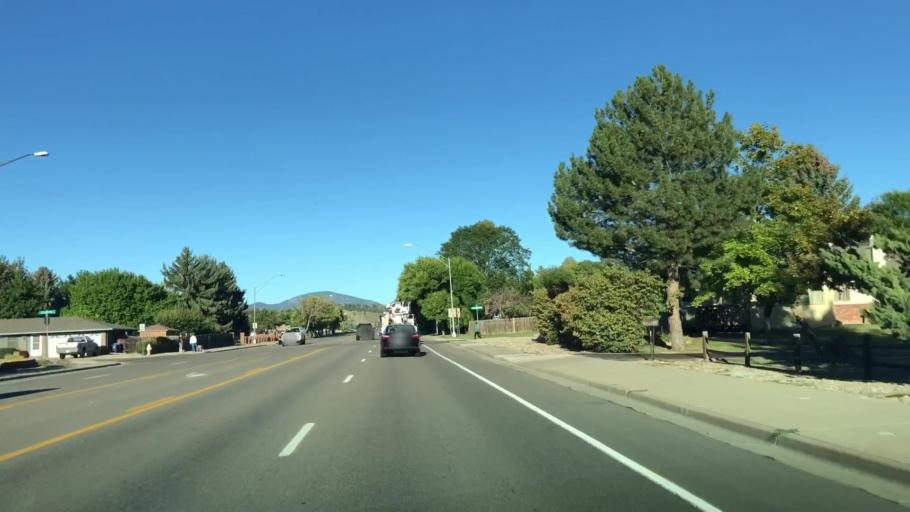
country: US
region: Colorado
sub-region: Larimer County
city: Loveland
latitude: 40.4219
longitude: -105.1120
